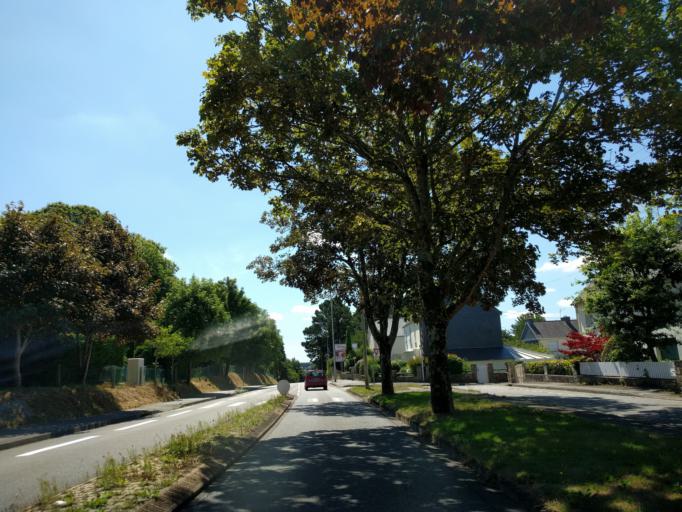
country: FR
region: Brittany
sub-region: Departement du Finistere
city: Quimper
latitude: 47.9844
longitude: -4.0985
